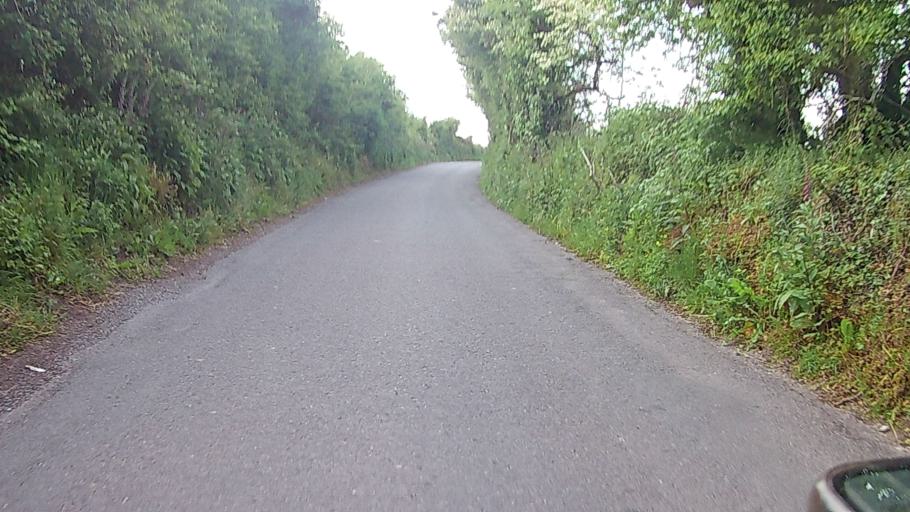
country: IE
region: Munster
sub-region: County Cork
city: Watergrasshill
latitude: 51.9690
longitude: -8.4113
